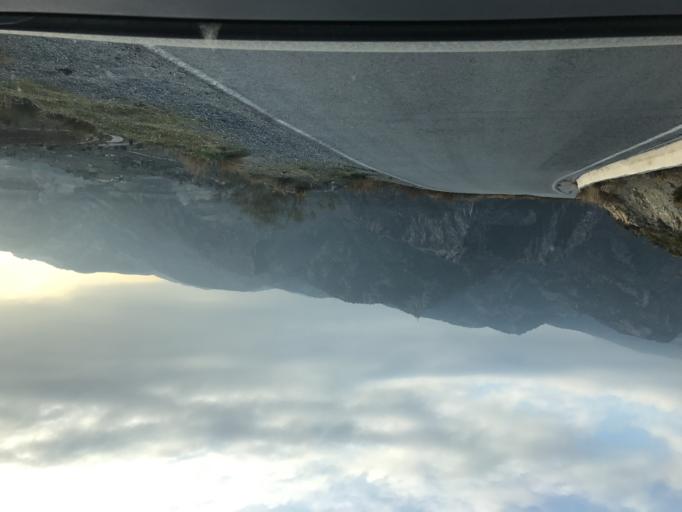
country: ES
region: Andalusia
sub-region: Provincia de Granada
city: Guejar-Sierra
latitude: 37.1682
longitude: -3.4453
